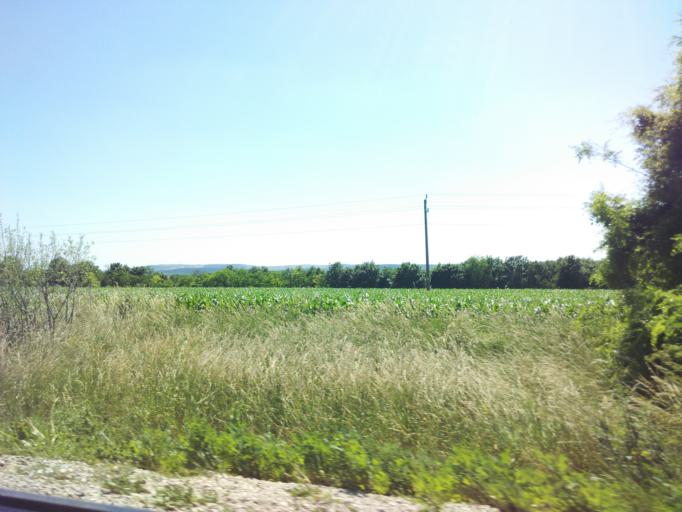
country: HU
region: Fejer
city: Kincsesbanya
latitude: 47.2841
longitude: 18.3111
